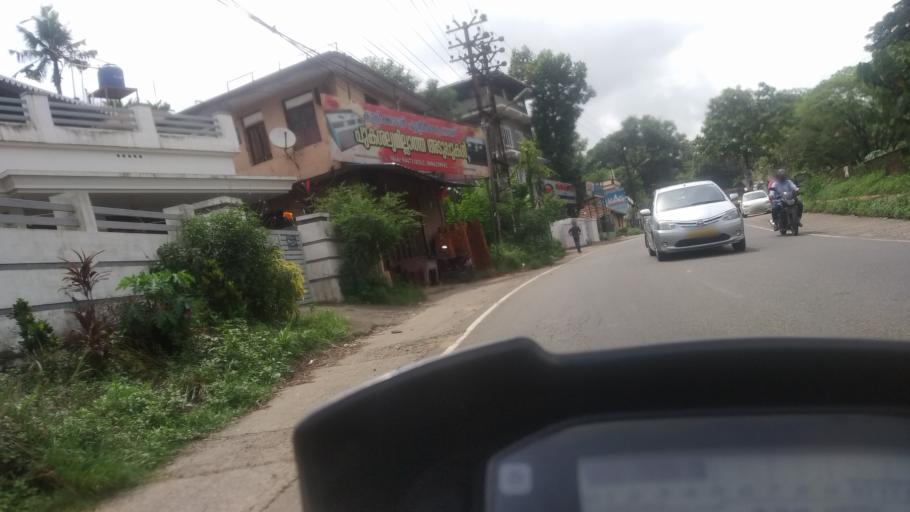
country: IN
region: Kerala
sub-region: Ernakulam
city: Aluva
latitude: 10.1219
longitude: 76.3361
